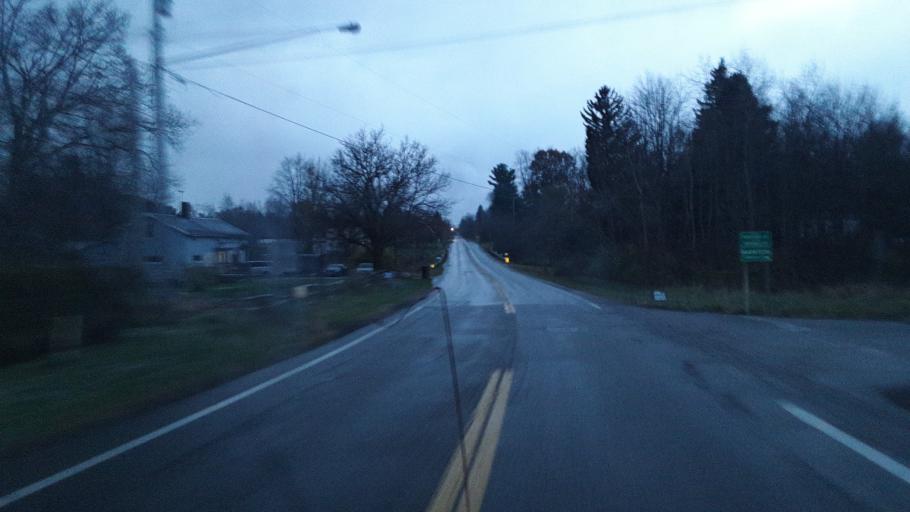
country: US
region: Ohio
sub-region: Portage County
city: Mantua
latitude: 41.3477
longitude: -81.2238
